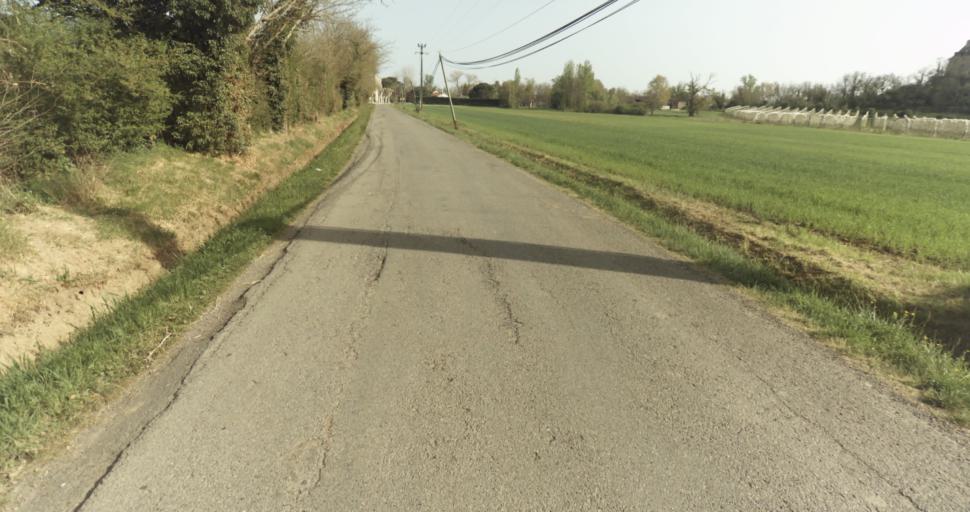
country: FR
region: Midi-Pyrenees
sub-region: Departement du Tarn-et-Garonne
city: Moissac
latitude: 44.1187
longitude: 1.1559
